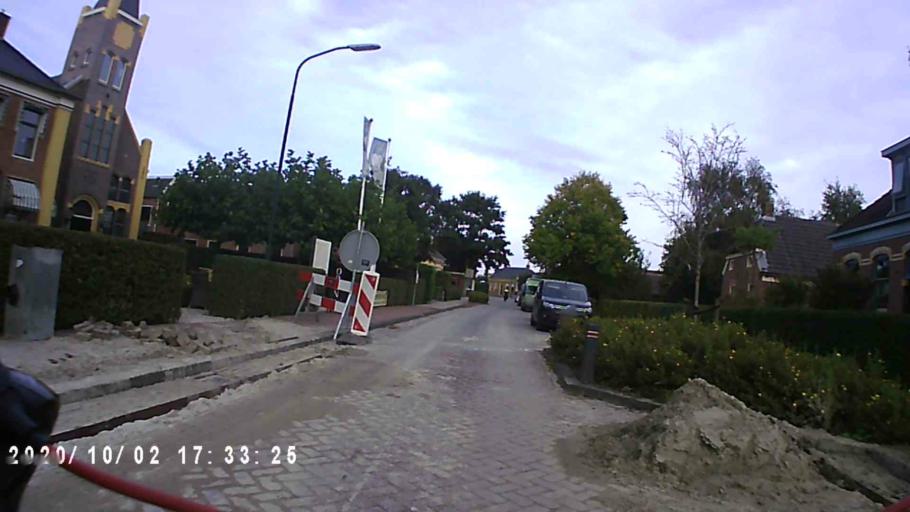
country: NL
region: Groningen
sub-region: Gemeente De Marne
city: Ulrum
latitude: 53.3355
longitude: 6.3399
